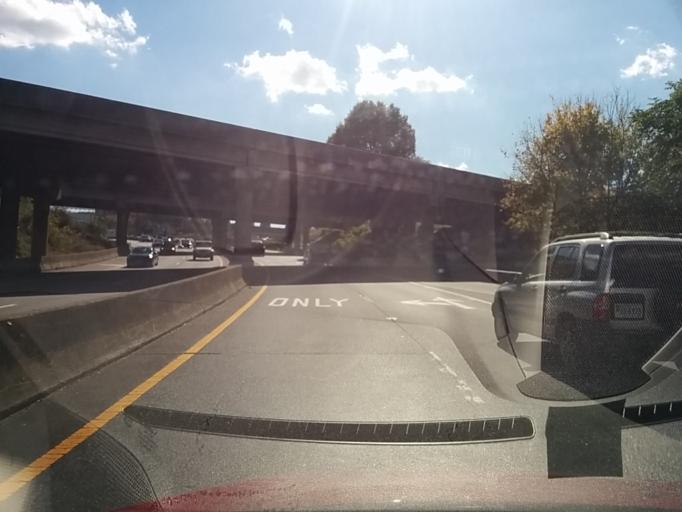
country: US
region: Virginia
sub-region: Botetourt County
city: Daleville
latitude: 37.3889
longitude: -79.9053
